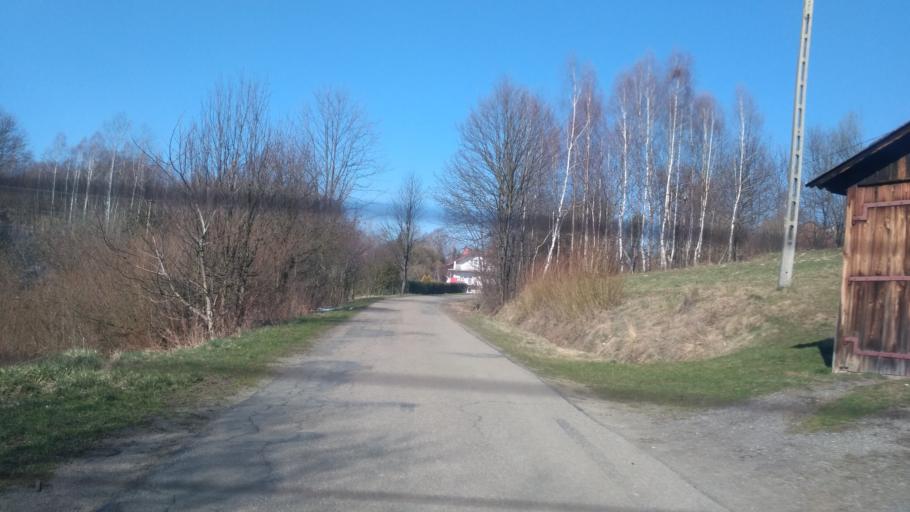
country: PL
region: Subcarpathian Voivodeship
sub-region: Powiat strzyzowski
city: Gwoznica Gorna
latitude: 49.8184
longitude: 22.0191
